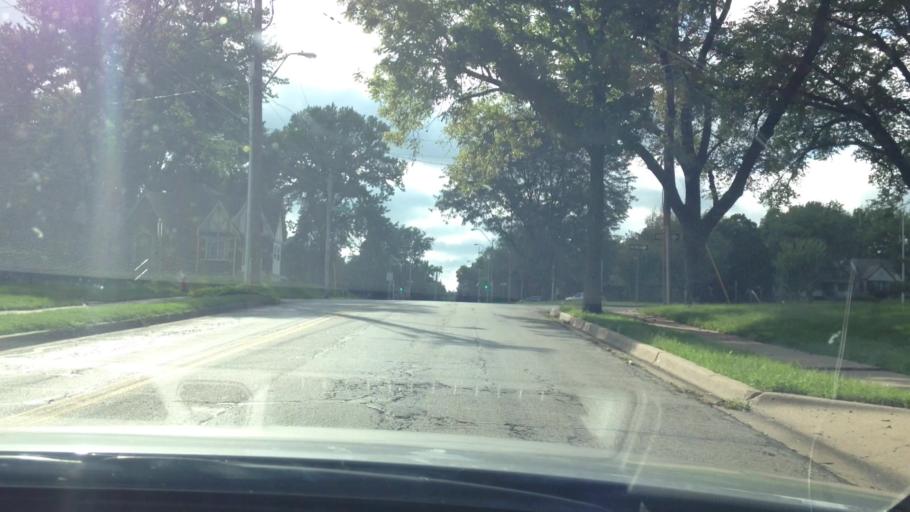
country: US
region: Kansas
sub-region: Johnson County
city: Mission Hills
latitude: 39.0198
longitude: -94.5679
